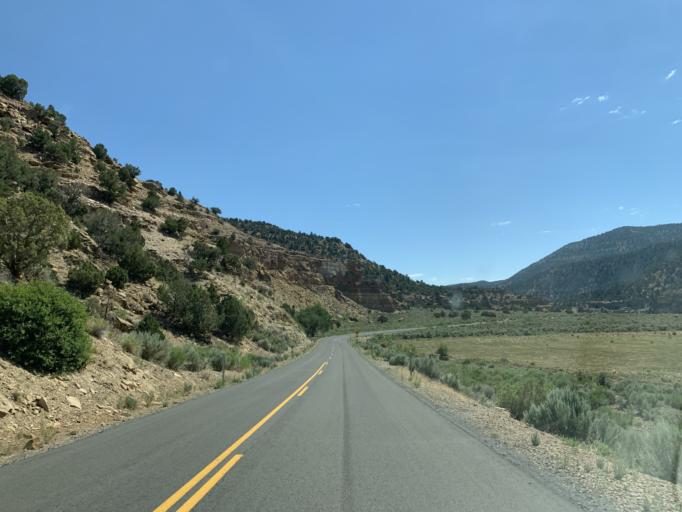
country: US
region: Utah
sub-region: Carbon County
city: East Carbon City
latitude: 39.7781
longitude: -110.4421
